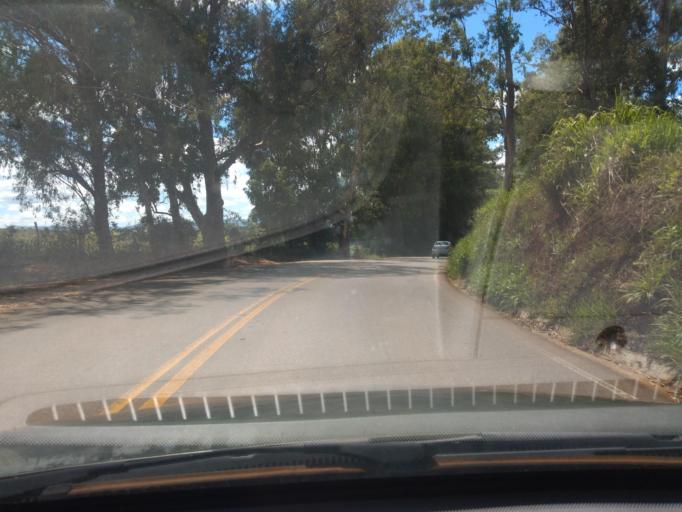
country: BR
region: Minas Gerais
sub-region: Tres Coracoes
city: Tres Coracoes
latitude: -21.6503
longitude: -45.1085
